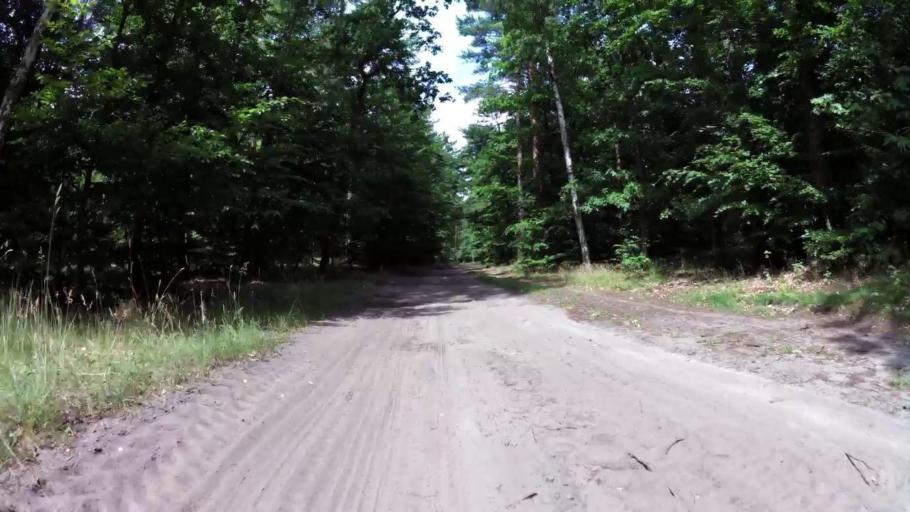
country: PL
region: West Pomeranian Voivodeship
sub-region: Powiat lobeski
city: Lobez
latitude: 53.5974
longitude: 15.6568
